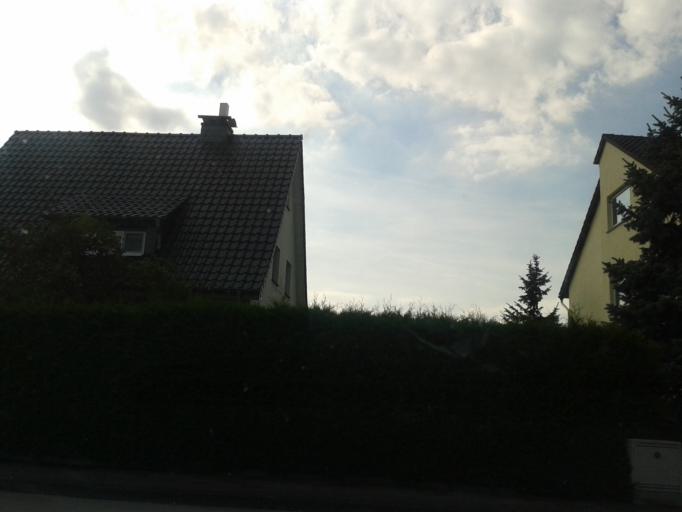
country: DE
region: North Rhine-Westphalia
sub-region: Regierungsbezirk Detmold
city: Schlangen
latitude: 51.8094
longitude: 8.8368
